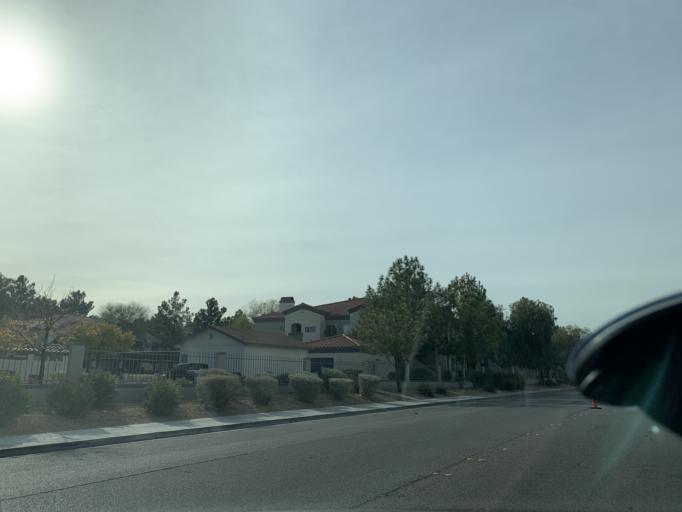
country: US
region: Nevada
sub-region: Clark County
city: Spring Valley
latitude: 36.0962
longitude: -115.2363
